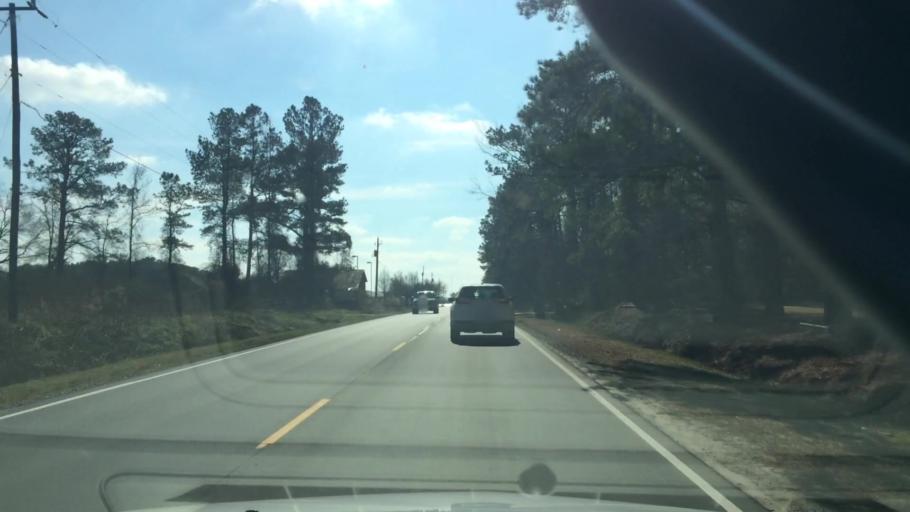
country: US
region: North Carolina
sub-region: Duplin County
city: Beulaville
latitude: 34.9331
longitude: -77.7713
